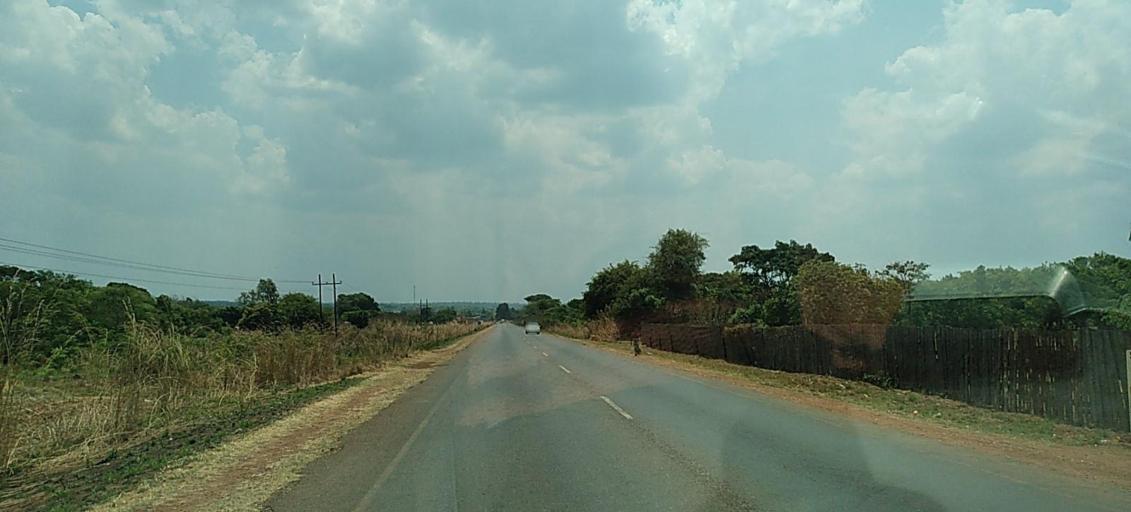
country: ZM
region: Copperbelt
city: Kalulushi
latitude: -12.8359
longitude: 27.9782
